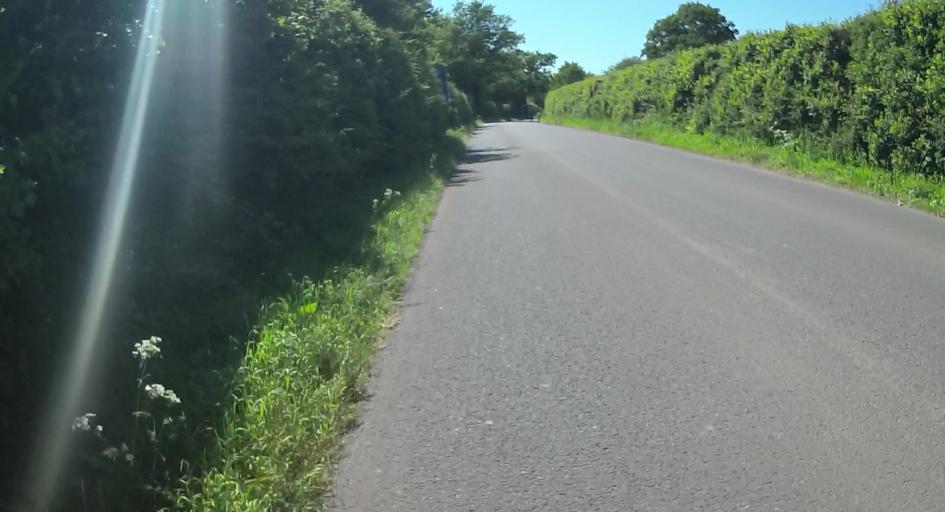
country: GB
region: England
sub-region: West Berkshire
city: Stratfield Mortimer
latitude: 51.3605
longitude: -0.9971
